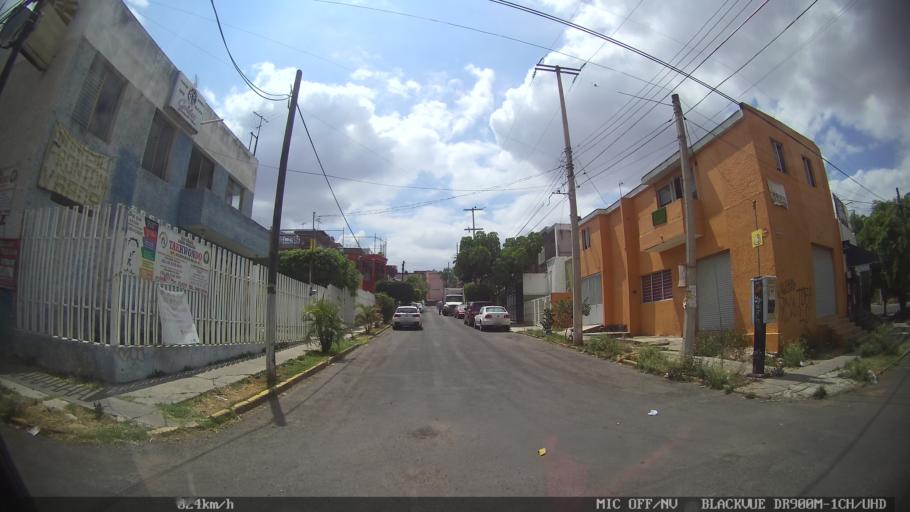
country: MX
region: Jalisco
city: Tonala
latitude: 20.6279
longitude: -103.2546
